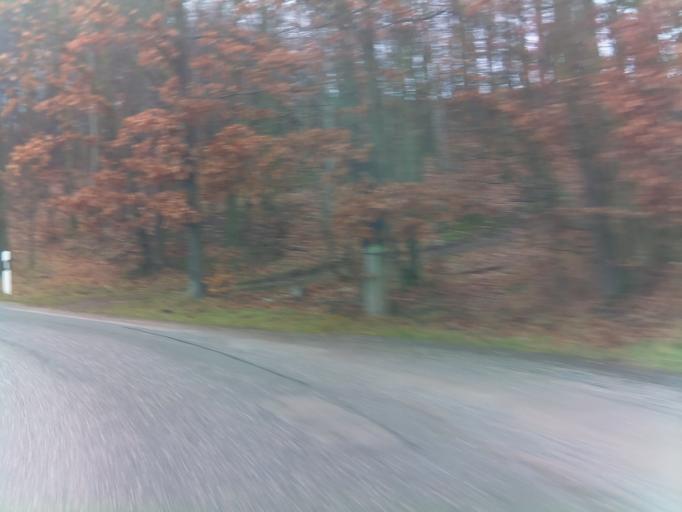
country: DE
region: Thuringia
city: Unterbodnitz
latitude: 50.8303
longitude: 11.6562
